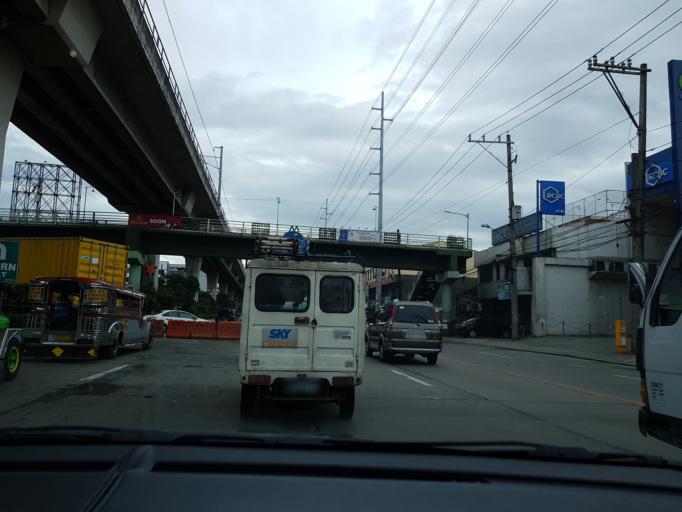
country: PH
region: Calabarzon
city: Del Monte
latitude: 14.6572
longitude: 120.9928
